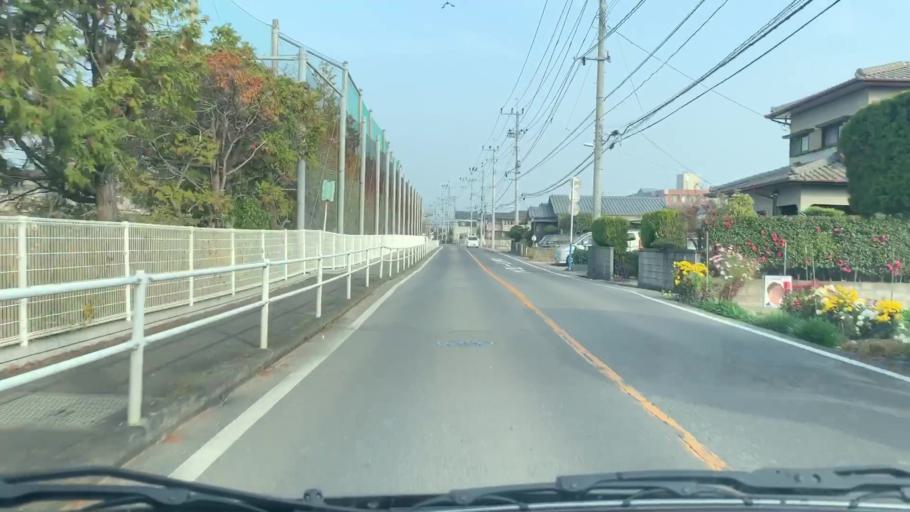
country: JP
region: Saga Prefecture
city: Saga-shi
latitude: 33.2397
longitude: 130.2585
